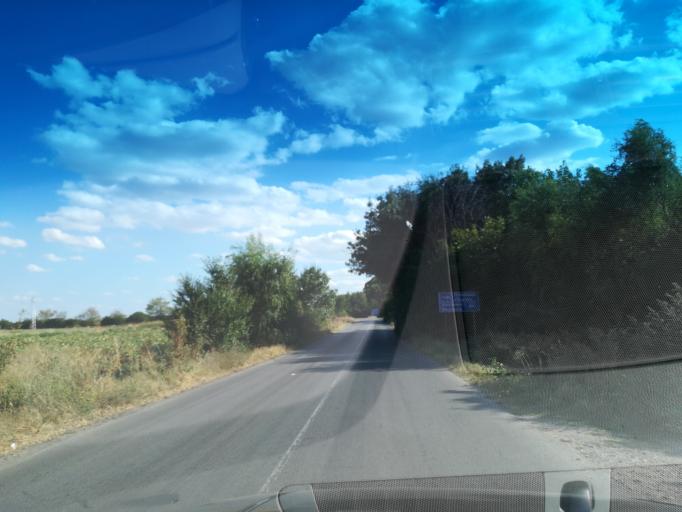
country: BG
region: Khaskovo
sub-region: Obshtina Mineralni Bani
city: Mineralni Bani
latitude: 42.0185
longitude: 25.4300
